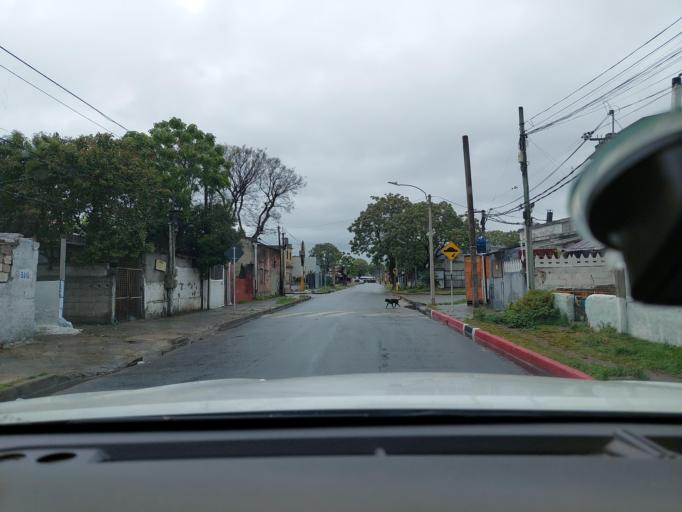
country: UY
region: Montevideo
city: Montevideo
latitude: -34.8641
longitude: -56.1453
